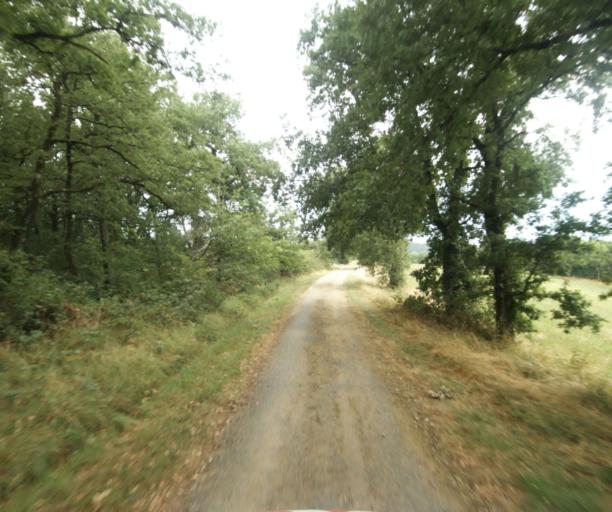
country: FR
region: Midi-Pyrenees
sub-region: Departement de la Haute-Garonne
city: Revel
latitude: 43.4140
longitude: 1.9820
